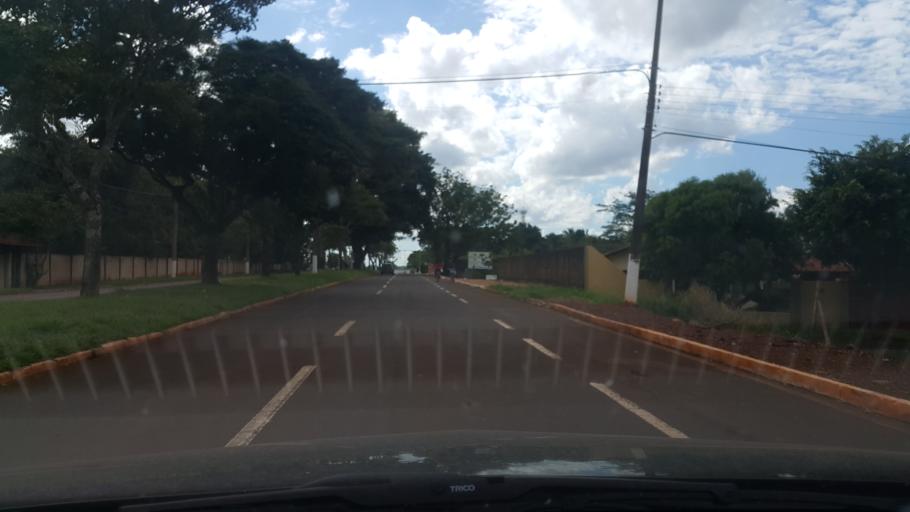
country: BR
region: Mato Grosso do Sul
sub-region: Dourados
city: Dourados
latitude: -22.2012
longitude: -54.8152
